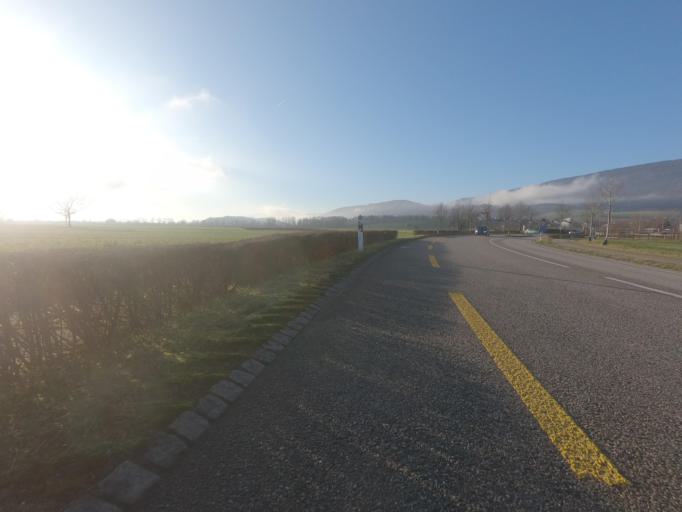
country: CH
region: Solothurn
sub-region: Bezirk Lebern
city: Grenchen
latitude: 47.1808
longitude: 7.4039
